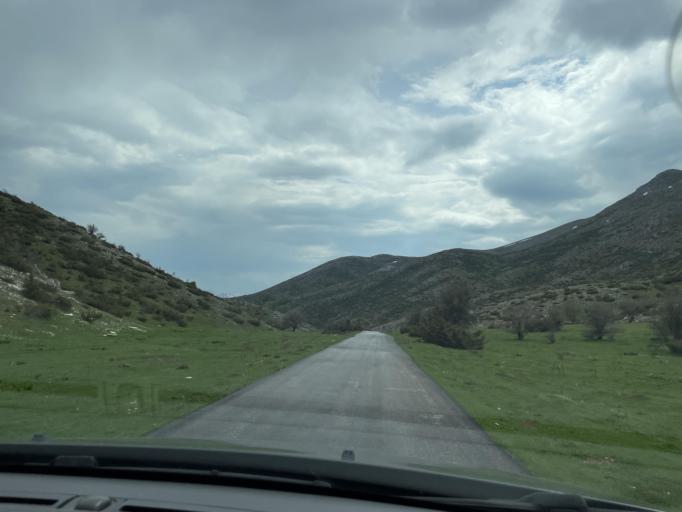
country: MK
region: Opstina Rostusa
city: Rostusha
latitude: 41.6183
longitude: 20.6846
